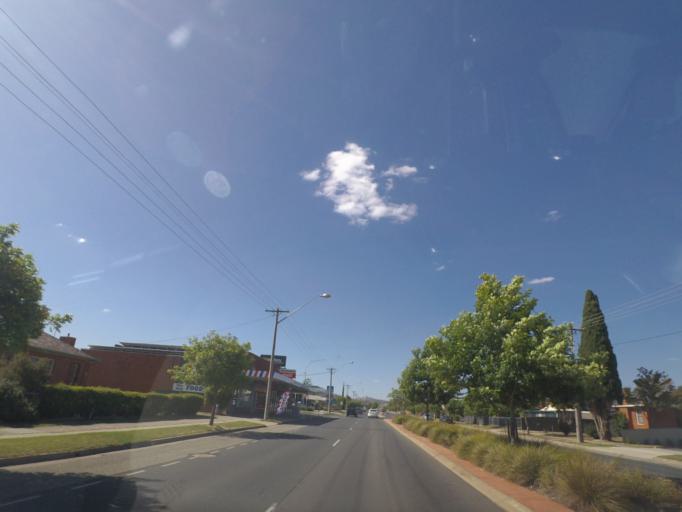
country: AU
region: New South Wales
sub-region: Albury Municipality
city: North Albury
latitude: -36.0584
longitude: 146.9324
